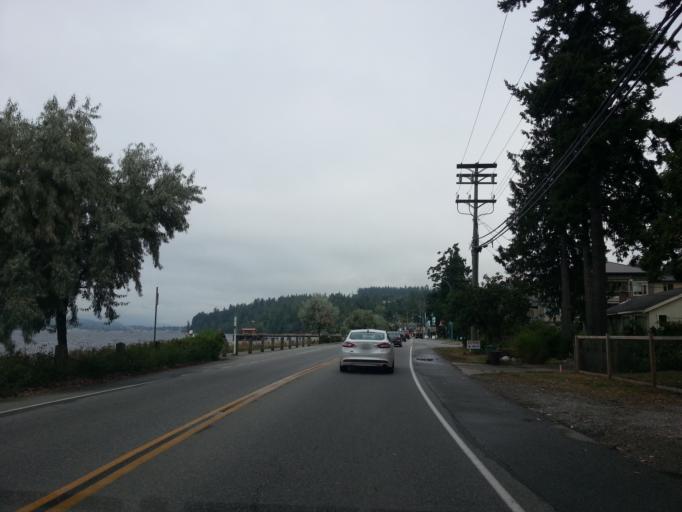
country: CA
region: British Columbia
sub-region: Sunshine Coast Regional District
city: Sechelt
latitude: 49.4427
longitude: -123.7284
